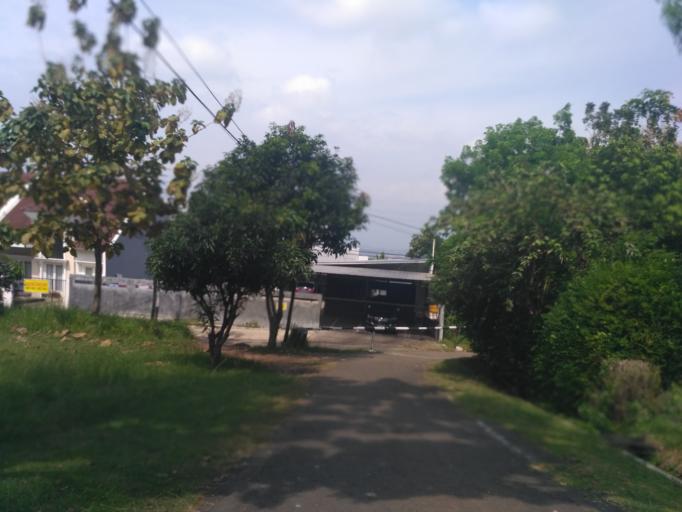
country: ID
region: Central Java
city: Semarang
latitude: -7.0448
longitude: 110.4252
